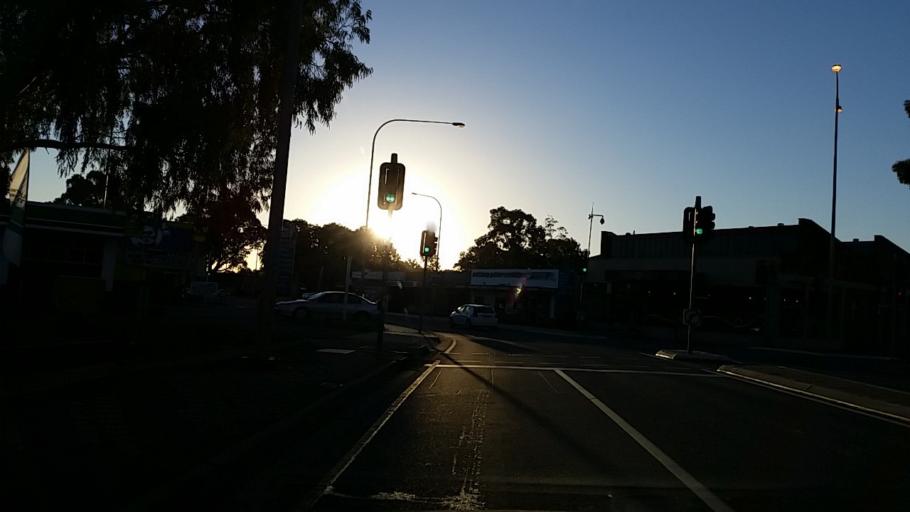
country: AU
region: South Australia
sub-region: Salisbury
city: Salisbury
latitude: -34.7641
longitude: 138.6445
